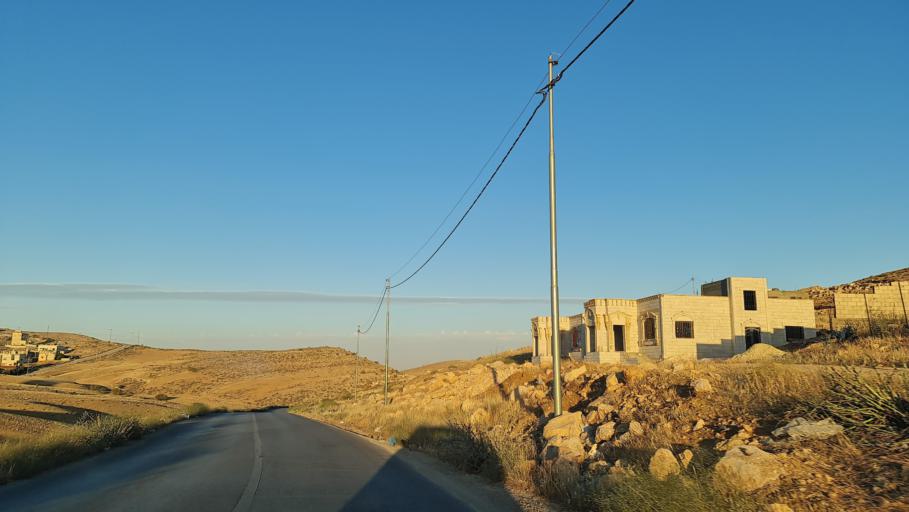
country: JO
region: Zarqa
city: Zarqa
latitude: 32.0838
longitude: 36.0308
